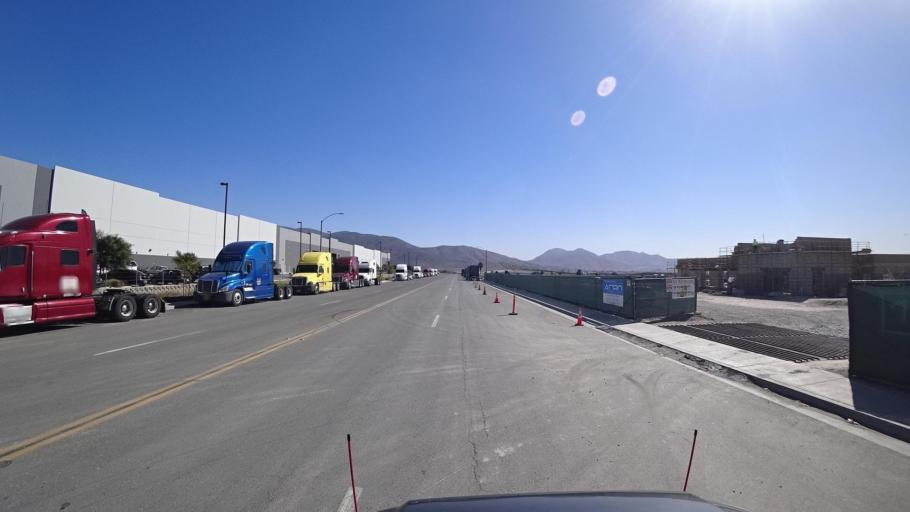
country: MX
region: Baja California
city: Tijuana
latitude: 32.5584
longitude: -116.9265
